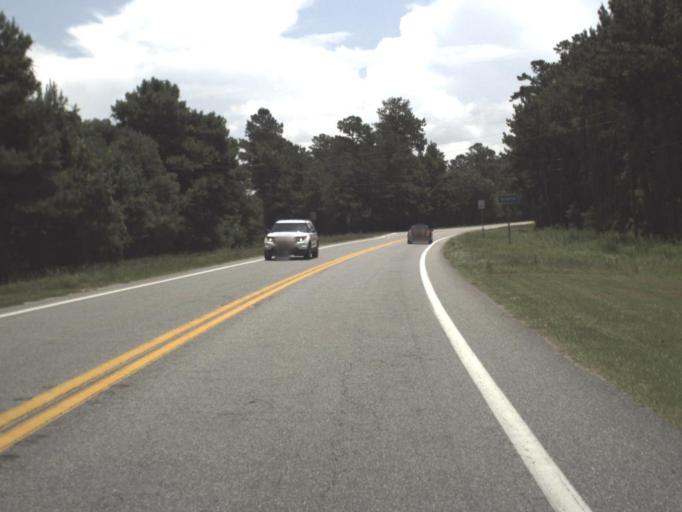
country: US
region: Florida
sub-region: Suwannee County
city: Live Oak
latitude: 30.3907
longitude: -83.1831
